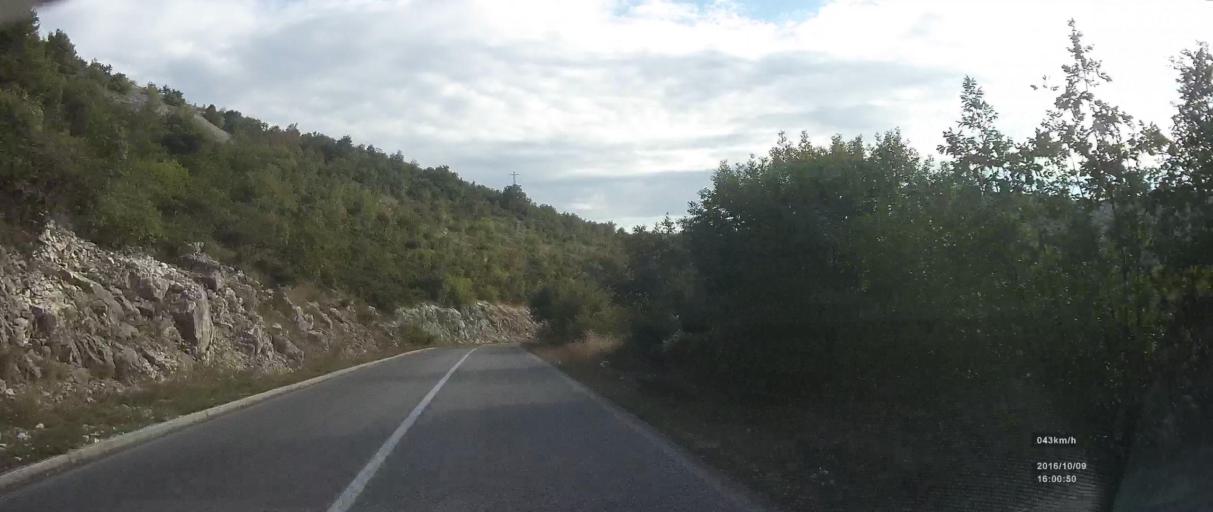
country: HR
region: Splitsko-Dalmatinska
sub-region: Grad Trogir
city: Trogir
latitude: 43.5686
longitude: 16.2466
